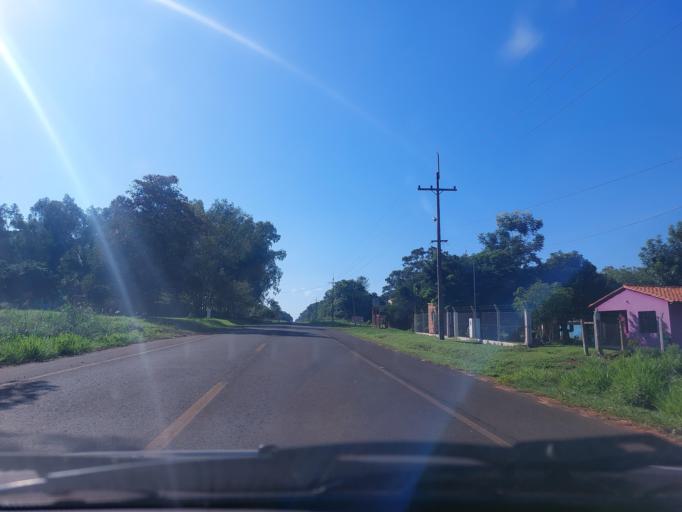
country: PY
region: San Pedro
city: Guayaybi
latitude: -24.5319
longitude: -56.4906
